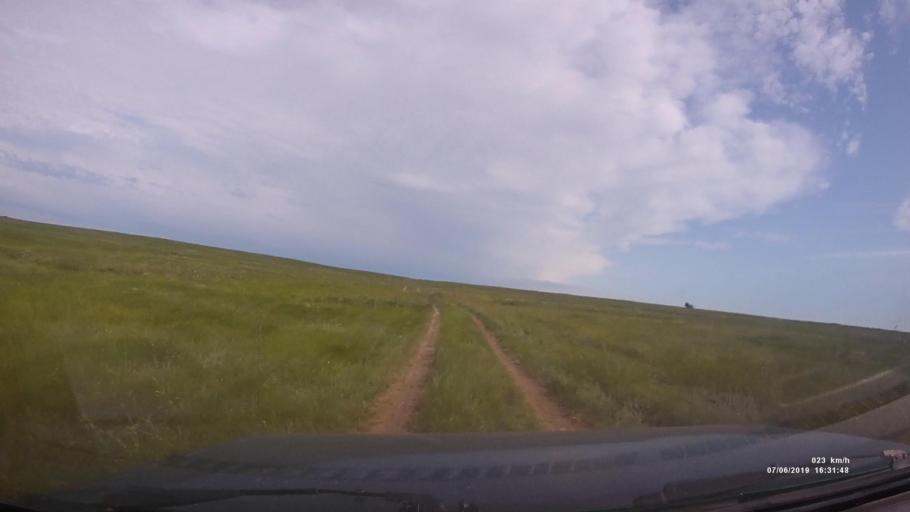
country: RU
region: Rostov
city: Staraya Stanitsa
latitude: 48.2552
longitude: 40.3279
